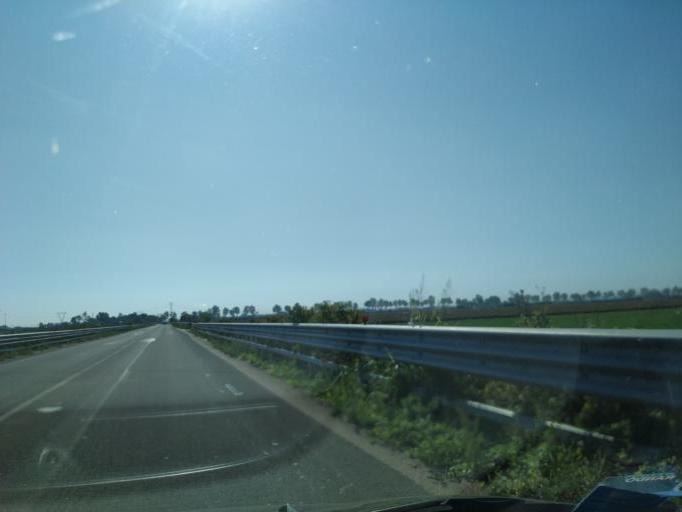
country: IT
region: Emilia-Romagna
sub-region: Provincia di Bologna
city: San Giovanni in Persiceto
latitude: 44.6760
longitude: 11.2012
